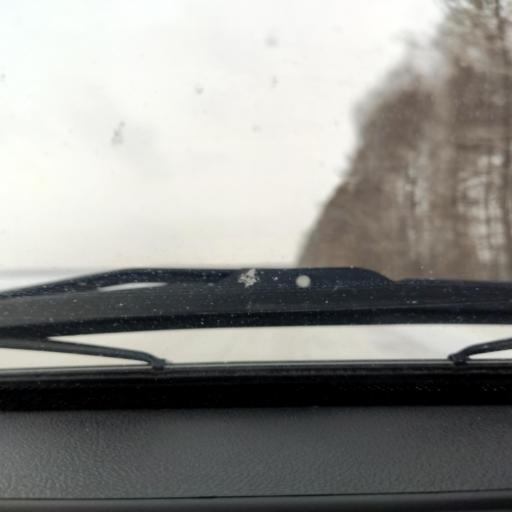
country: RU
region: Bashkortostan
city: Mikhaylovka
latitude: 54.8542
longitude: 55.8690
